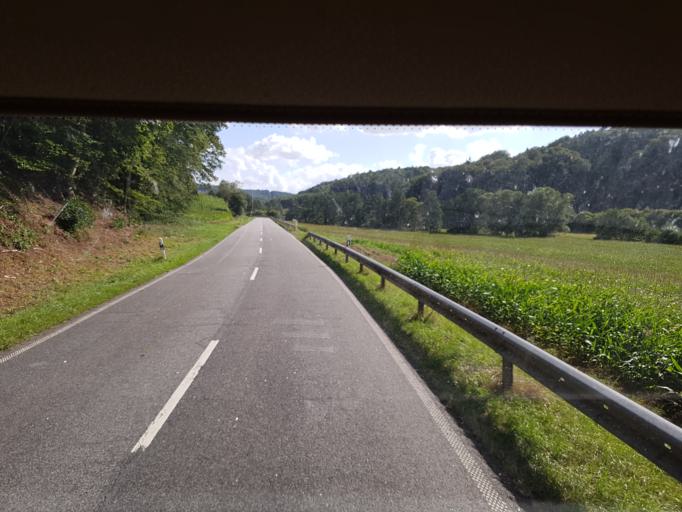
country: DE
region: Rheinland-Pfalz
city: Mannebach
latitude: 49.6288
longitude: 6.5115
